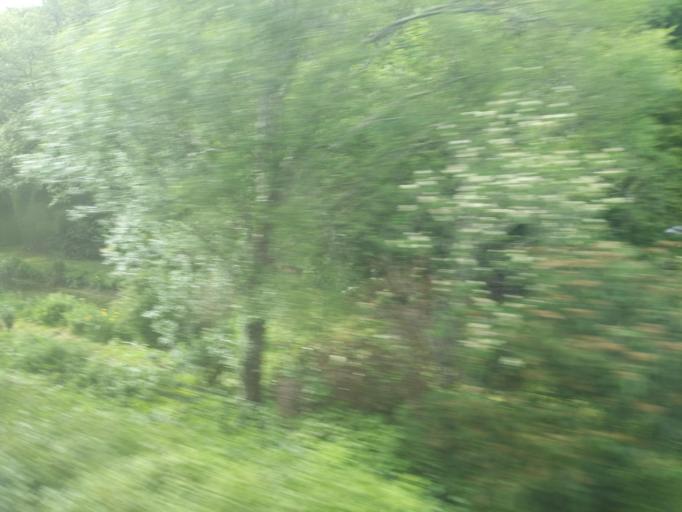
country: GB
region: England
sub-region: Devon
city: Barnstaple
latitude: 50.9823
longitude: -3.9755
